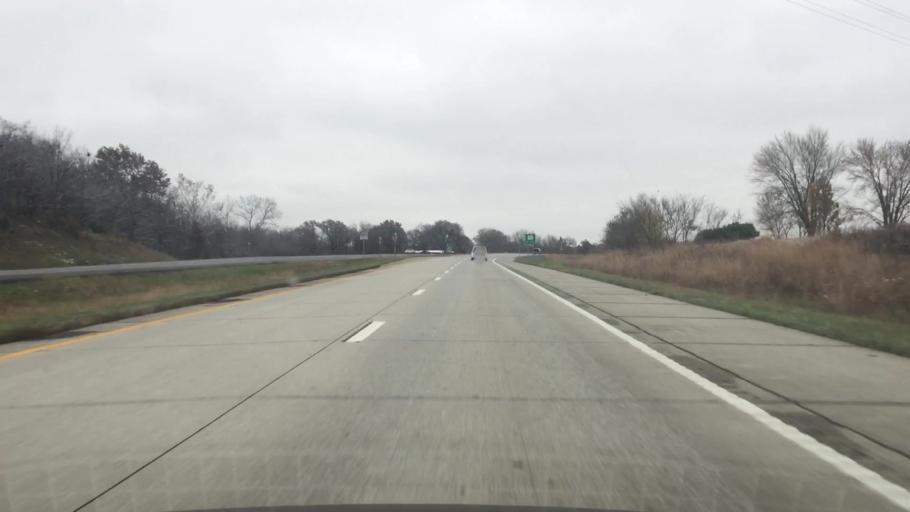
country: US
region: Missouri
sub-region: Saint Clair County
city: Osceola
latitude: 38.0140
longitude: -93.6609
